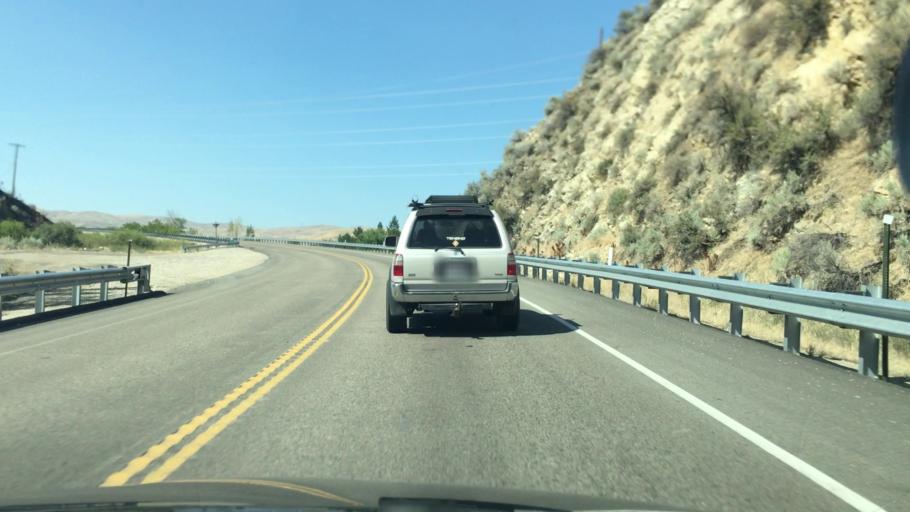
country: US
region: Idaho
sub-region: Ada County
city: Eagle
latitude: 43.7626
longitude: -116.2655
